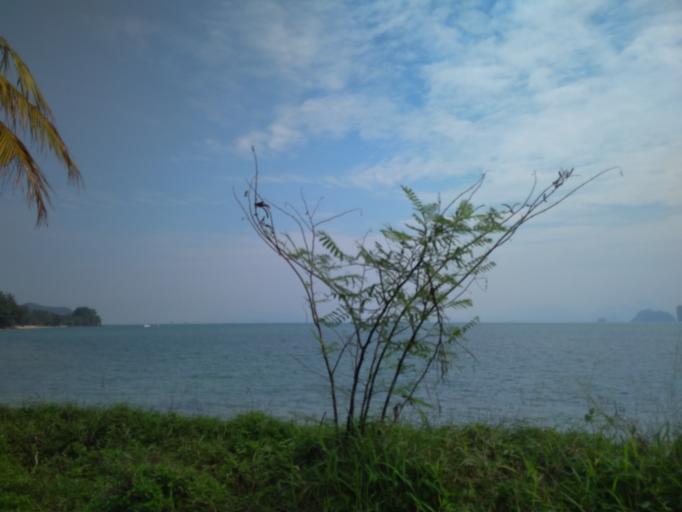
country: TH
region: Phangnga
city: Ko Yao
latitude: 8.1083
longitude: 98.6227
